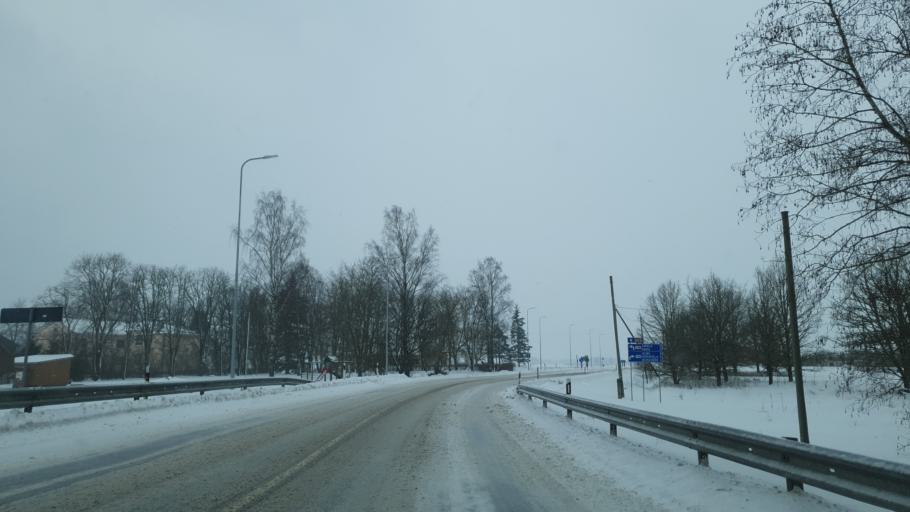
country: EE
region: Jaervamaa
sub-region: Jaerva-Jaani vald
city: Jarva-Jaani
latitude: 59.1903
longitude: 25.7641
